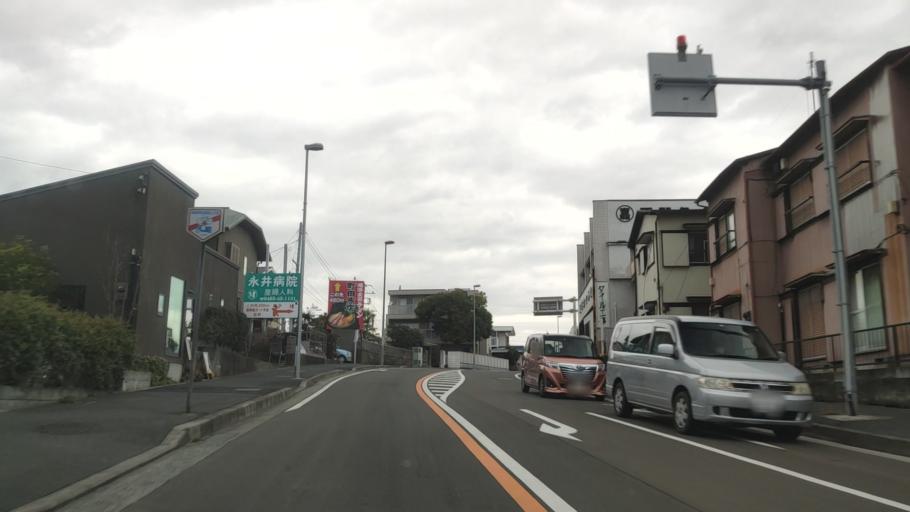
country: JP
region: Kanagawa
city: Odawara
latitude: 35.2757
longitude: 139.1778
